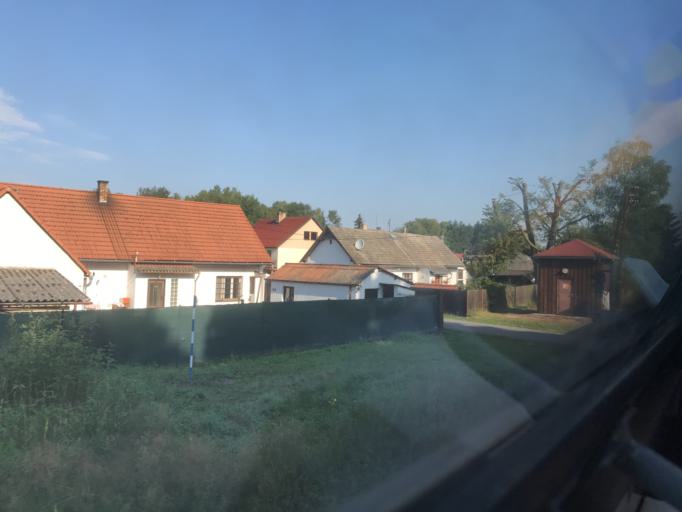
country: CZ
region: Jihocesky
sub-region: Okres Tabor
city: Veseli nad Luznici
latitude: 49.1523
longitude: 14.7261
